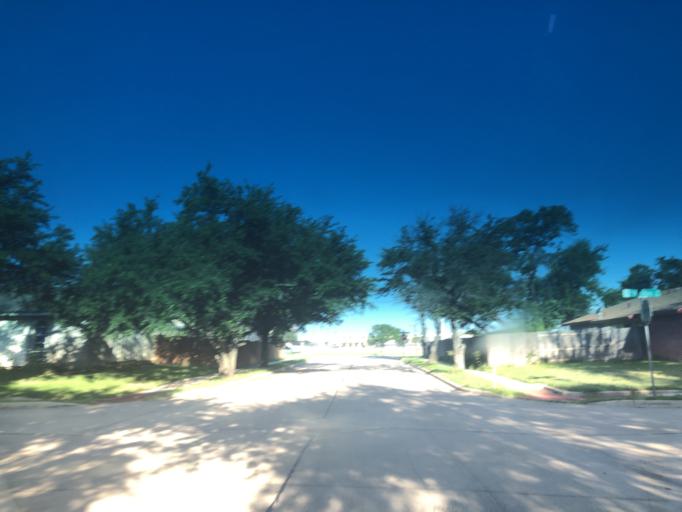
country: US
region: Texas
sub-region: Dallas County
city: Grand Prairie
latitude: 32.6967
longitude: -97.0023
